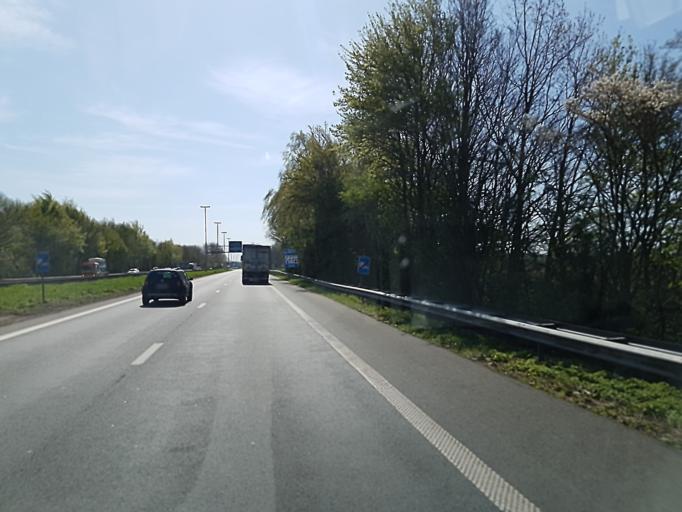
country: FR
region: Nord-Pas-de-Calais
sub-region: Departement du Nord
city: Camphin-en-Pevele
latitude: 50.6211
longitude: 3.3182
